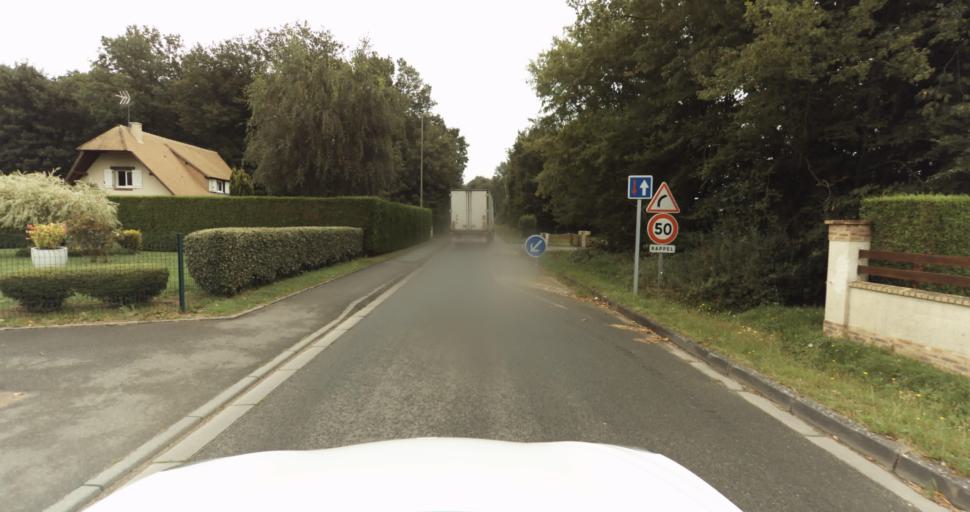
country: FR
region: Haute-Normandie
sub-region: Departement de l'Eure
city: Aviron
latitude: 49.0492
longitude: 1.1272
